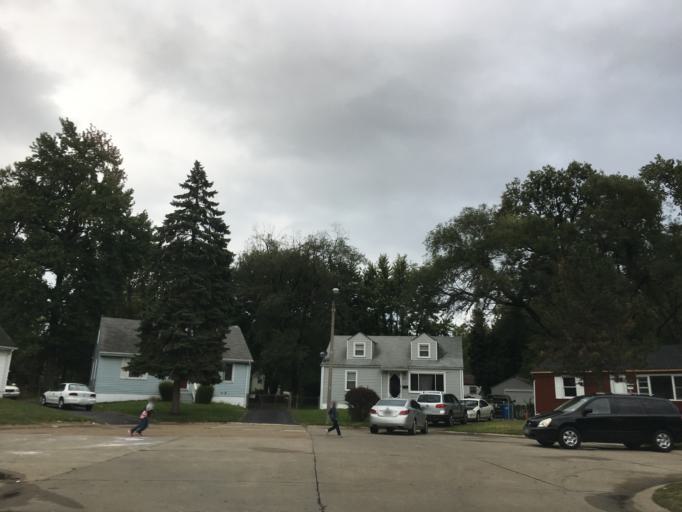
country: US
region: Missouri
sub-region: Saint Louis County
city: Berkeley
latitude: 38.7639
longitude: -90.3333
